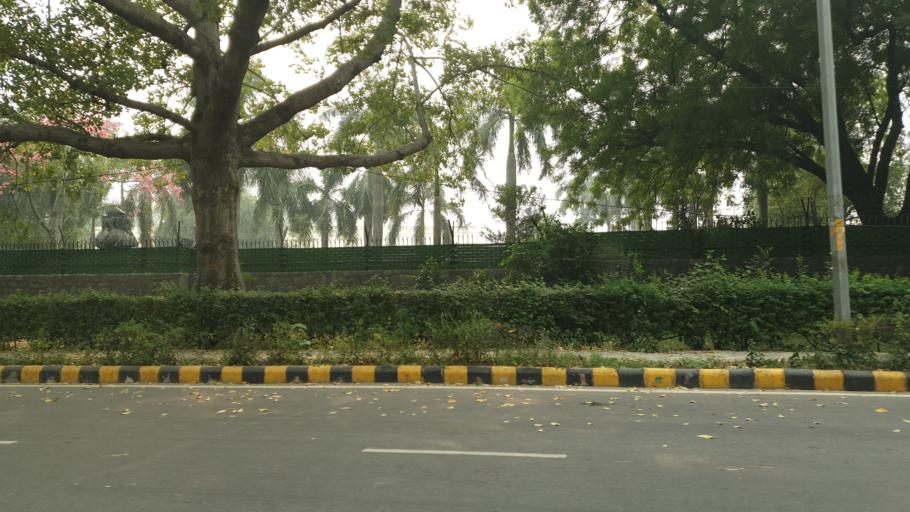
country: IN
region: NCT
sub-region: New Delhi
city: New Delhi
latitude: 28.5853
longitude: 77.1864
